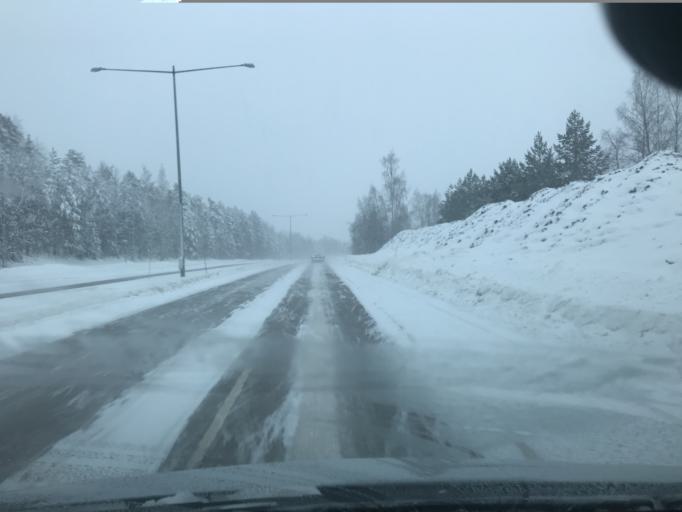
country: SE
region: Norrbotten
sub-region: Lulea Kommun
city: Lulea
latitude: 65.6095
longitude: 22.1365
